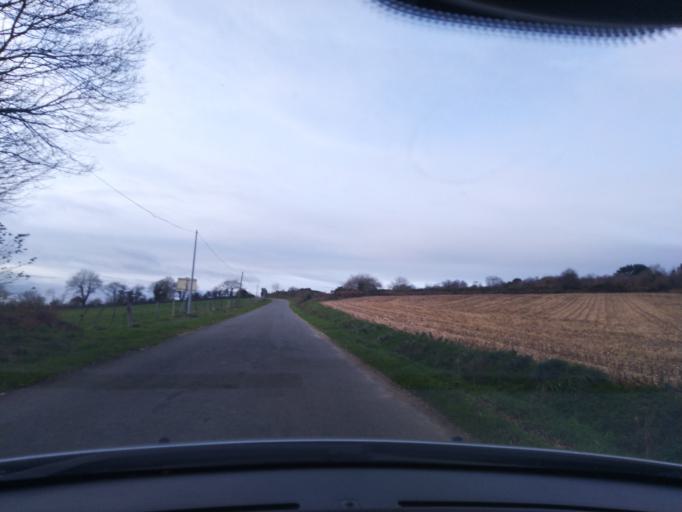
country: FR
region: Brittany
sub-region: Departement du Finistere
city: Guerlesquin
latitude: 48.5221
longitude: -3.5972
